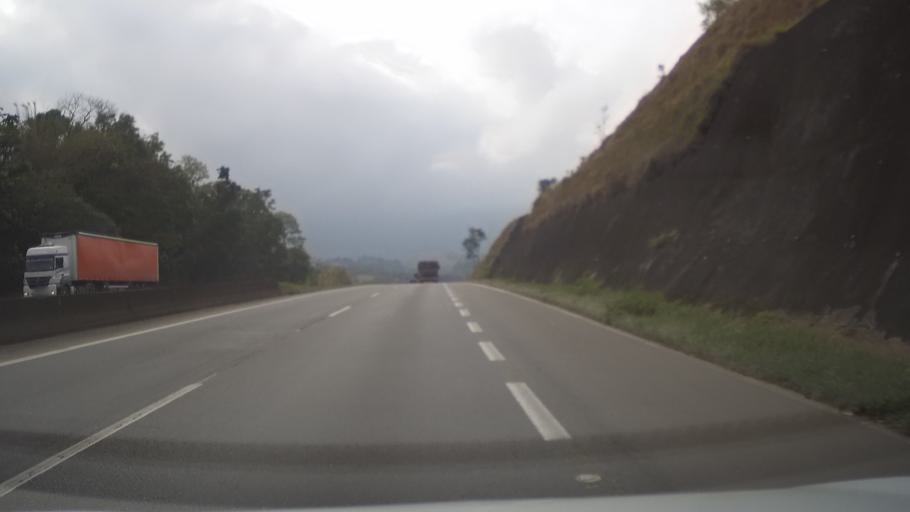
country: BR
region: Minas Gerais
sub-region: Extrema
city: Extrema
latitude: -22.8785
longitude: -46.3965
